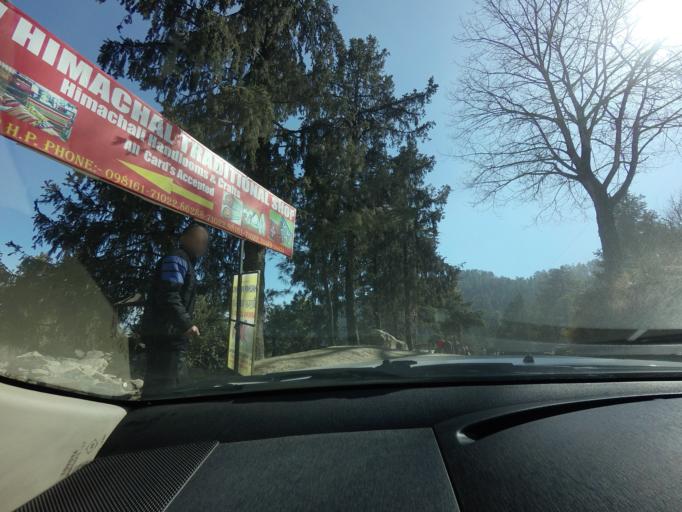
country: IN
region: Himachal Pradesh
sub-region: Shimla
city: Theog
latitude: 31.0982
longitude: 77.2677
